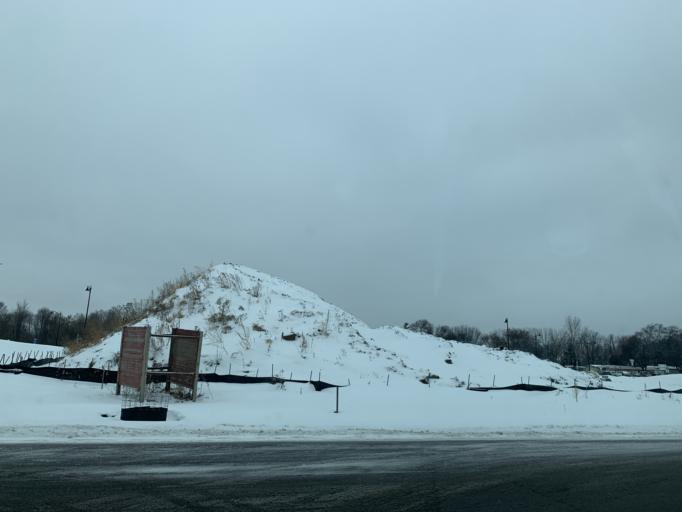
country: US
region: Minnesota
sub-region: Ramsey County
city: North Saint Paul
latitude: 45.0283
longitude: -92.9727
